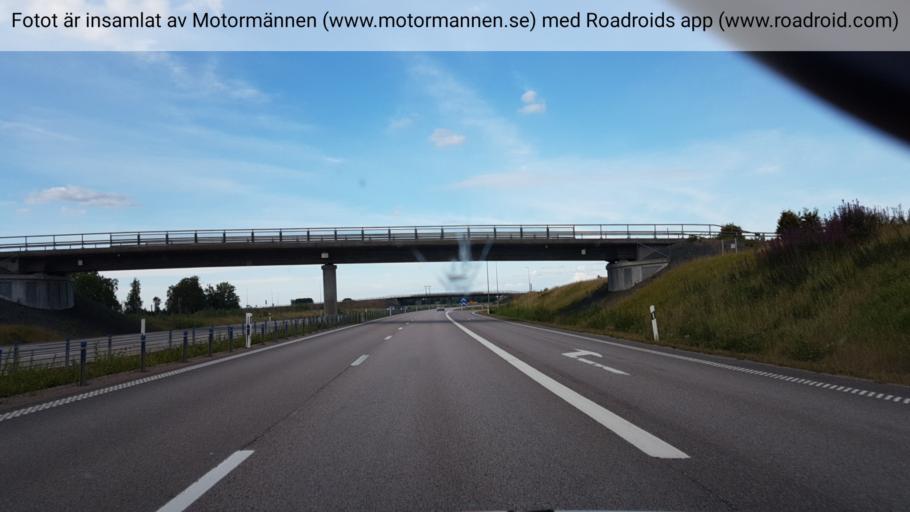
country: SE
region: Vaestra Goetaland
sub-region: Gotene Kommun
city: Goetene
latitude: 58.5315
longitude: 13.5192
